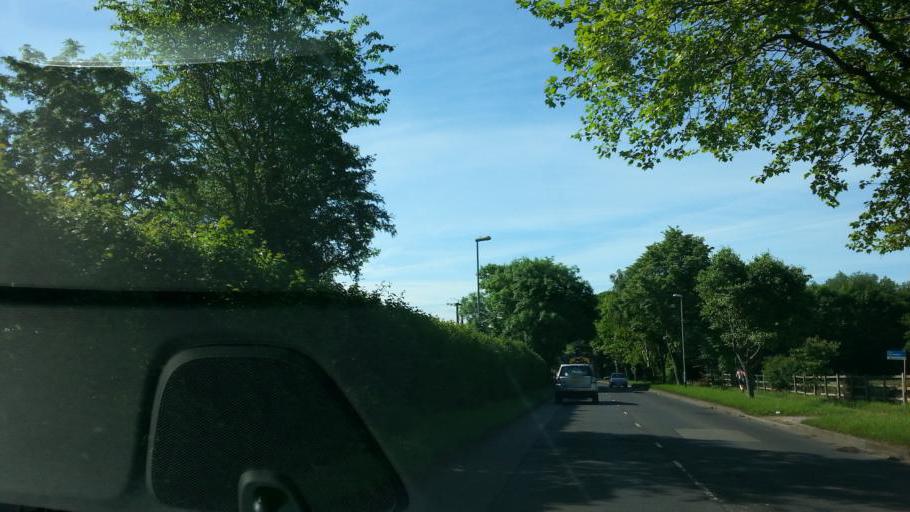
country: GB
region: England
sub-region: Nottinghamshire
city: Hucknall
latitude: 53.0533
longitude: -1.1828
